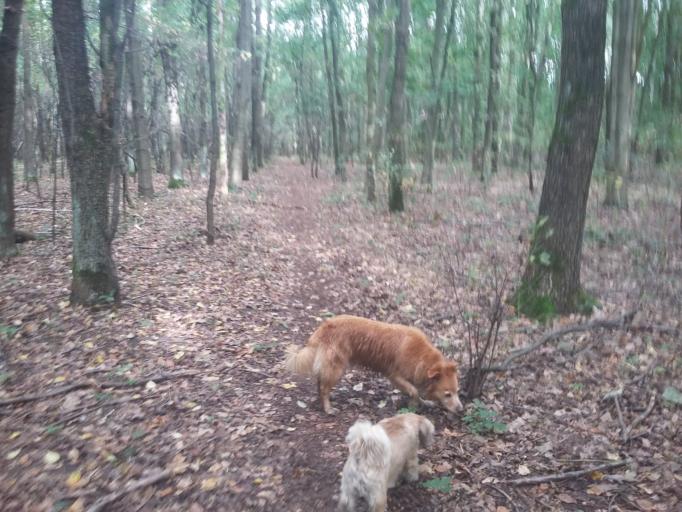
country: PL
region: Lodz Voivodeship
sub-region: Powiat pabianicki
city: Ksawerow
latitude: 51.7279
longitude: 19.3904
